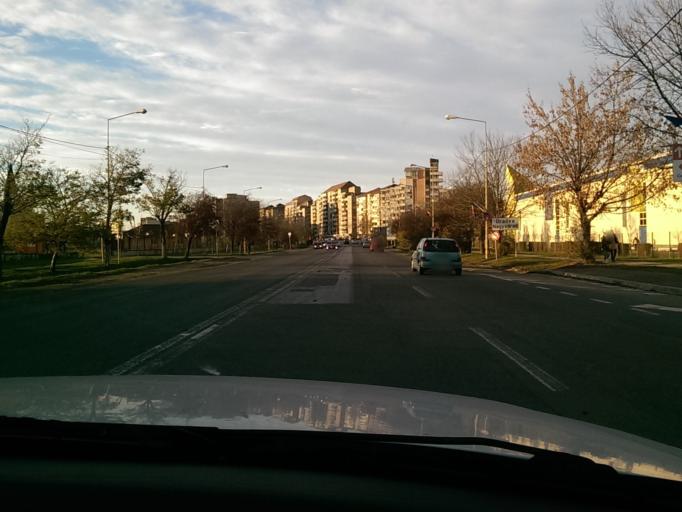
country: RO
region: Bihor
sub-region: Comuna Sanmartin
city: Sanmartin
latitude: 47.0270
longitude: 21.9577
